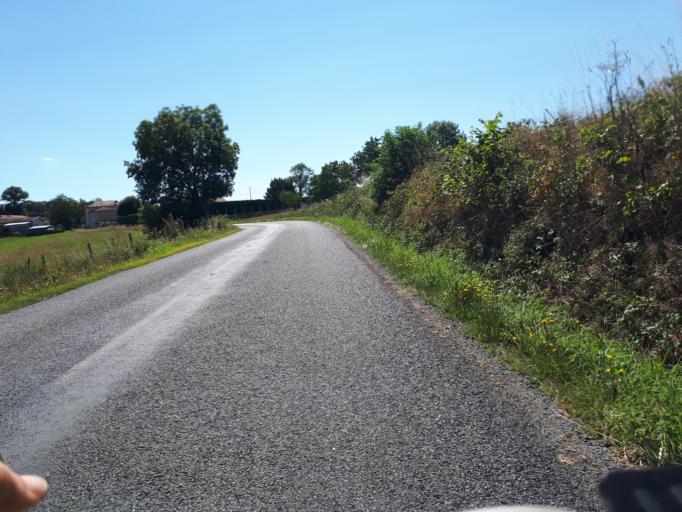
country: FR
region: Rhone-Alpes
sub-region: Departement de la Loire
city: Panissieres
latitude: 45.8067
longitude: 4.3355
